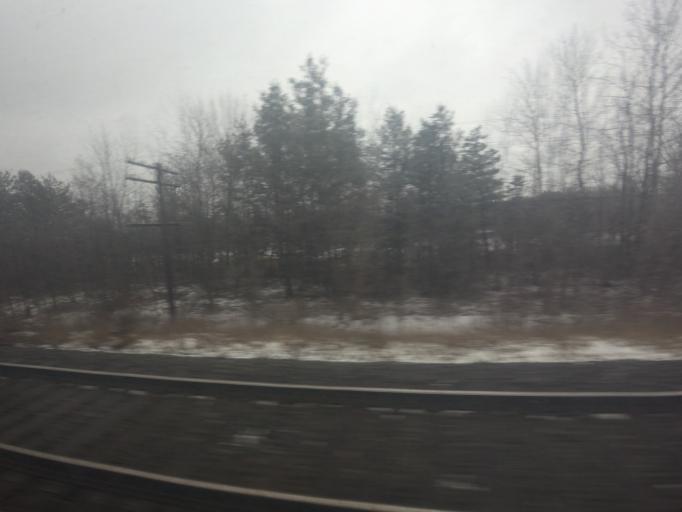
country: CA
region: Ontario
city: Quinte West
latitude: 44.0605
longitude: -77.6768
